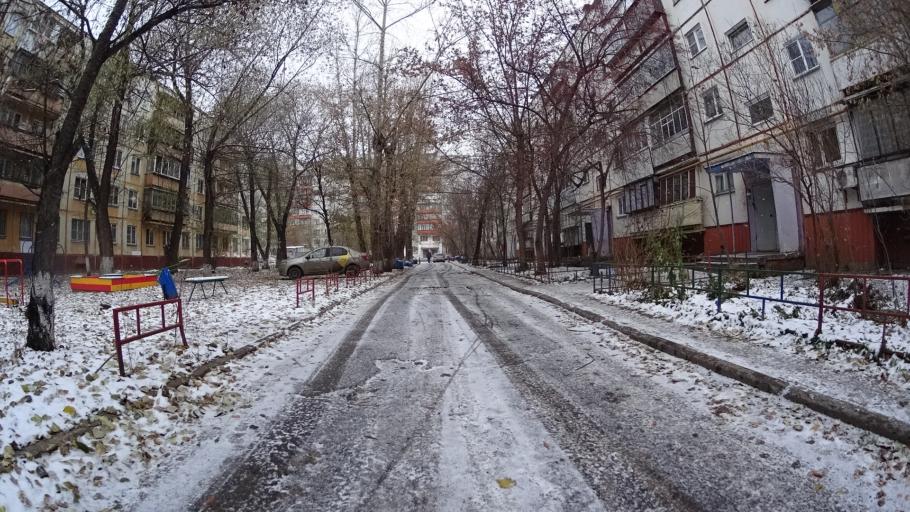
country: RU
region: Chelyabinsk
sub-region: Gorod Chelyabinsk
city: Chelyabinsk
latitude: 55.1928
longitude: 61.3172
